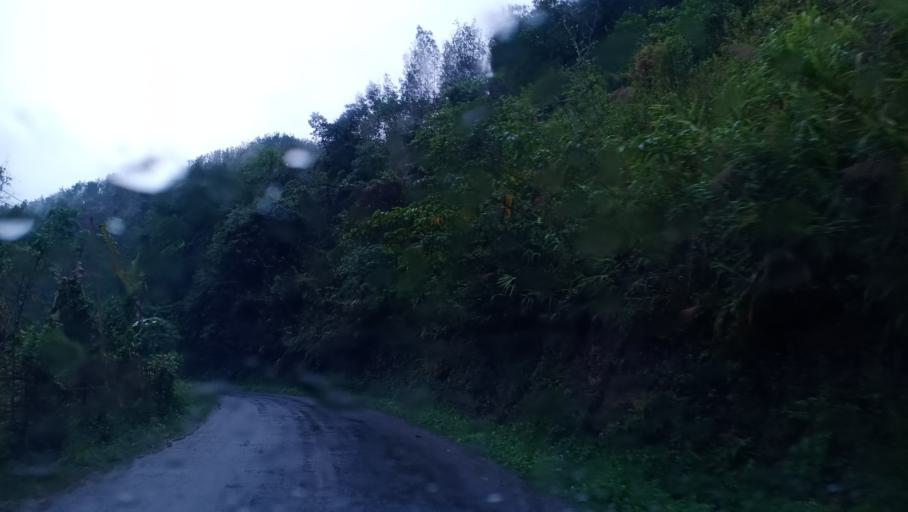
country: LA
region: Phongsali
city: Khoa
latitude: 21.0663
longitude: 102.4871
